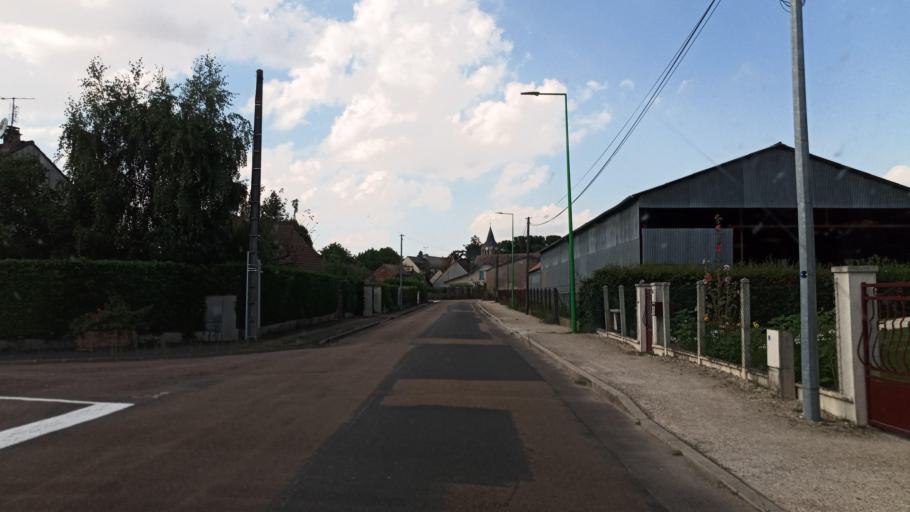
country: FR
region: Bourgogne
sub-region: Departement de l'Yonne
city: Saint-Valerien
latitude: 48.1766
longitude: 3.0967
